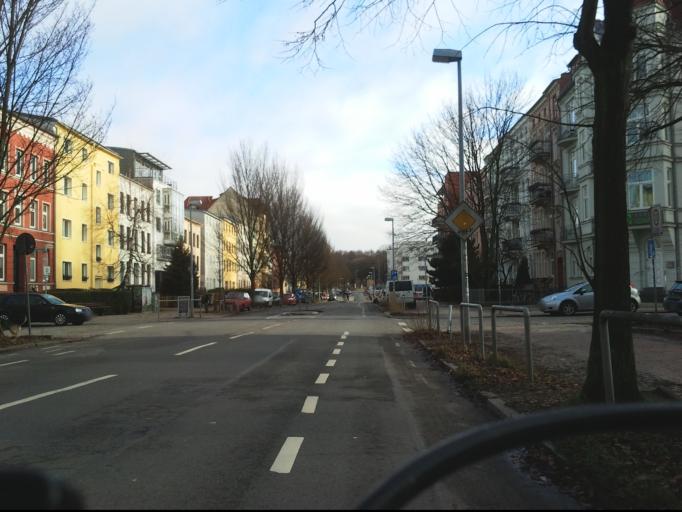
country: DE
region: Mecklenburg-Vorpommern
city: Rostock
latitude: 54.0867
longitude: 12.1110
